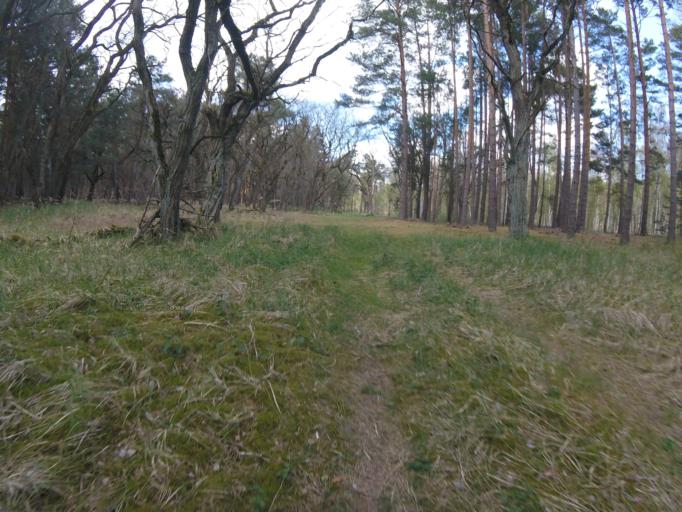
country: DE
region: Brandenburg
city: Munchehofe
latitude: 52.2054
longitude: 13.7746
